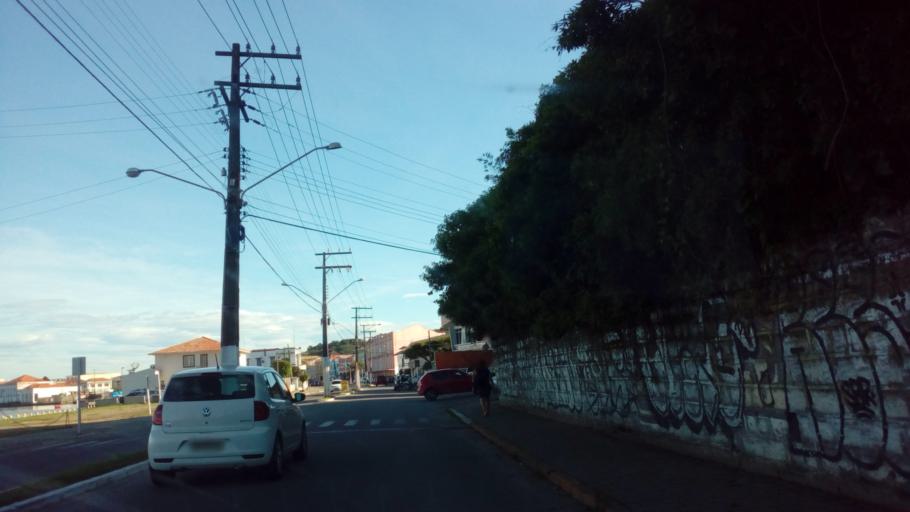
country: BR
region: Santa Catarina
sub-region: Laguna
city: Laguna
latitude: -28.4869
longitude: -48.7831
